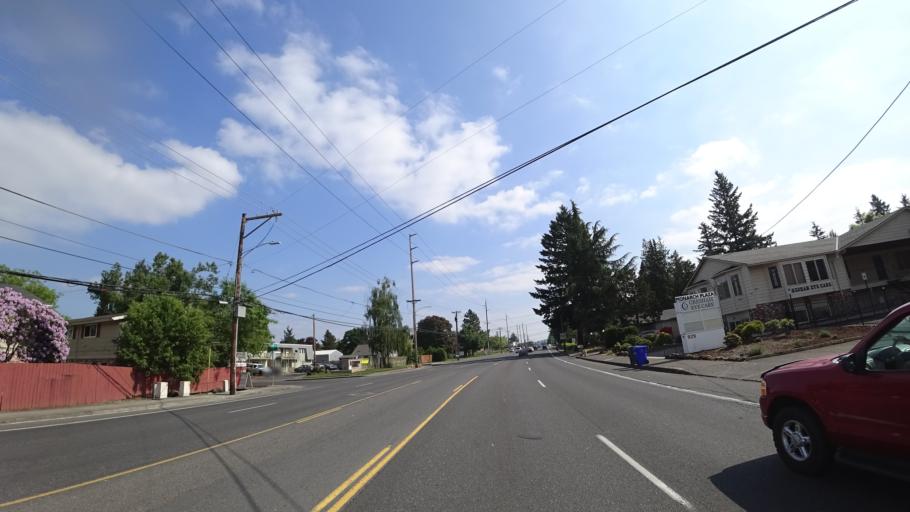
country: US
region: Oregon
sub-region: Multnomah County
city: Fairview
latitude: 45.5302
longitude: -122.4771
